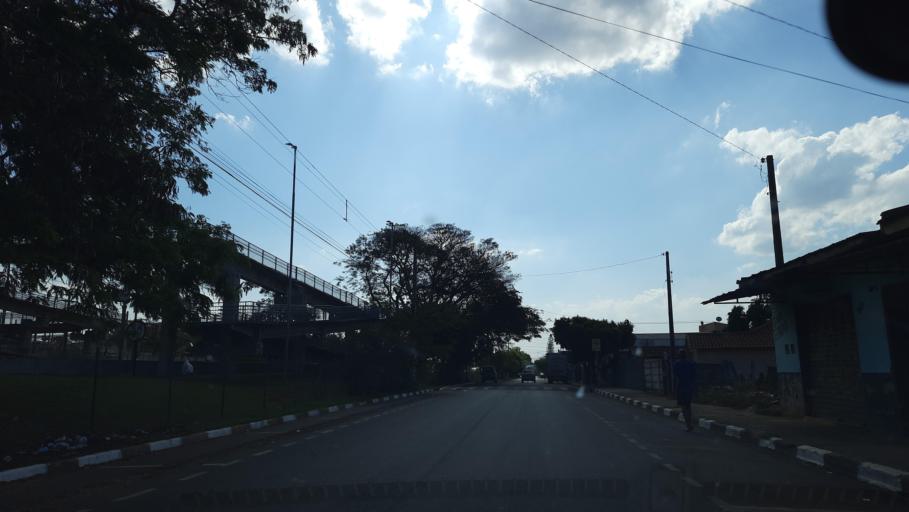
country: BR
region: Sao Paulo
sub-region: Vargem Grande Do Sul
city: Vargem Grande do Sul
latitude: -21.8419
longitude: -46.9039
